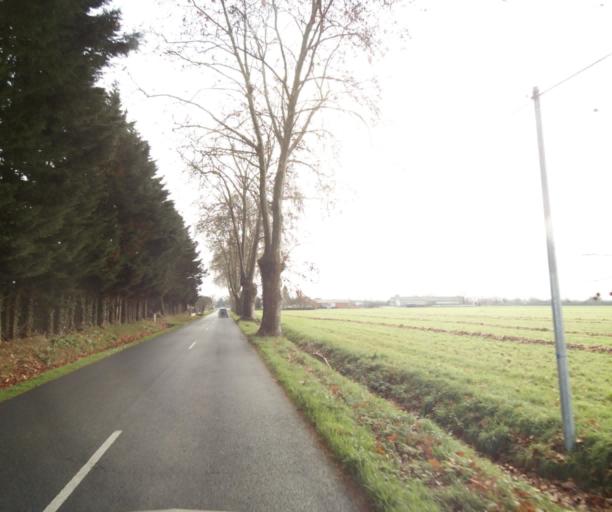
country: FR
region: Midi-Pyrenees
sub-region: Departement de la Haute-Garonne
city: Villemur-sur-Tarn
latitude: 43.8766
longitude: 1.4875
